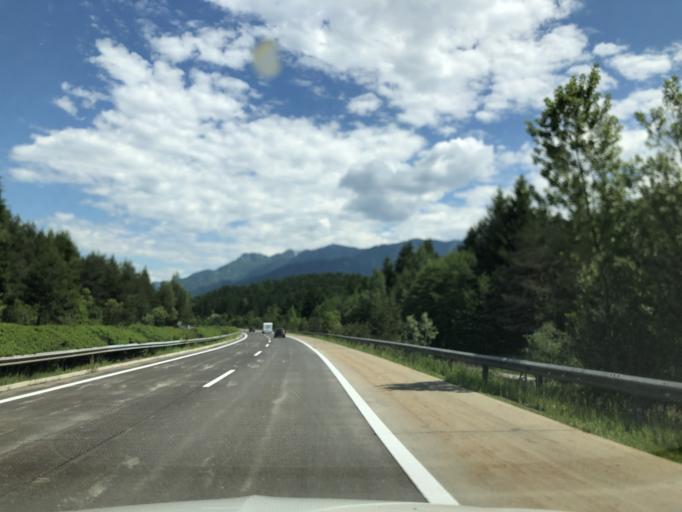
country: AT
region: Carinthia
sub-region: Politischer Bezirk Villach Land
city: Arnoldstein
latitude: 46.5585
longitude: 13.7486
